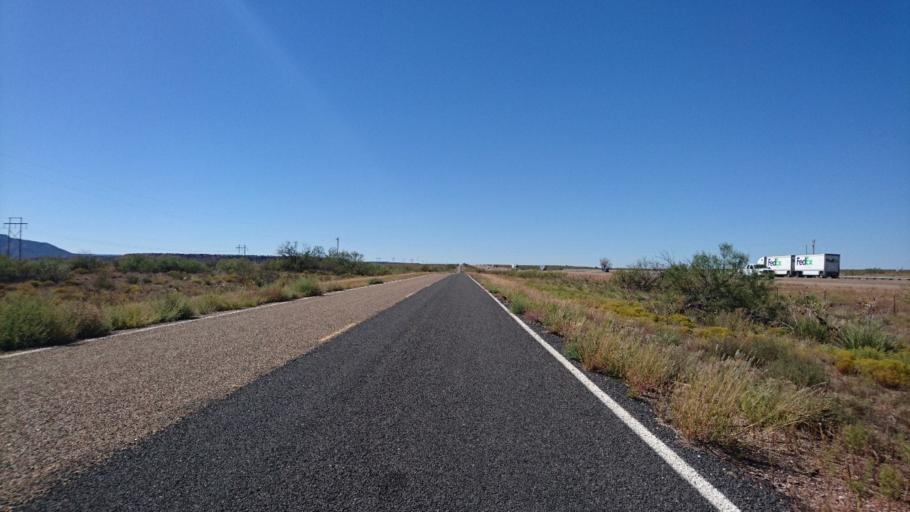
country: US
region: New Mexico
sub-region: Quay County
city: Tucumcari
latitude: 35.0842
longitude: -104.1057
